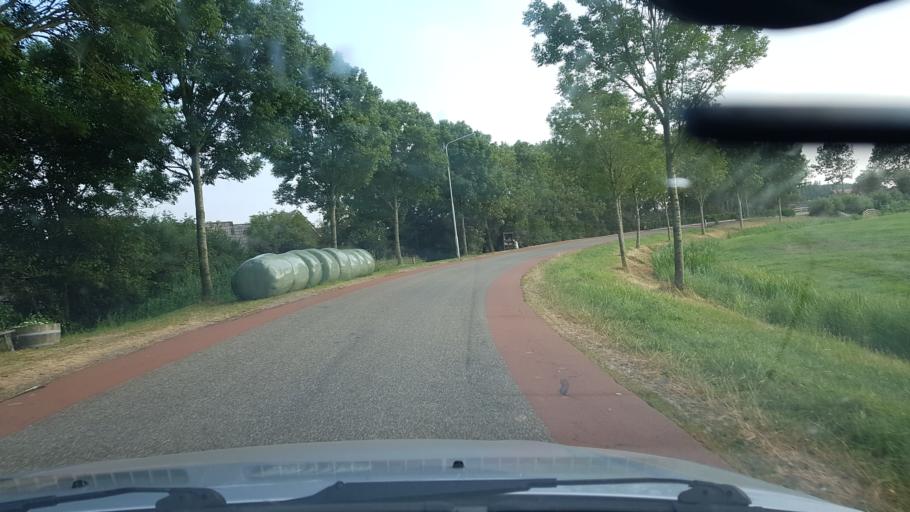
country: NL
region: Friesland
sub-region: Gemeente Ferwerderadiel
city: Burdaard
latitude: 53.3104
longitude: 5.8779
